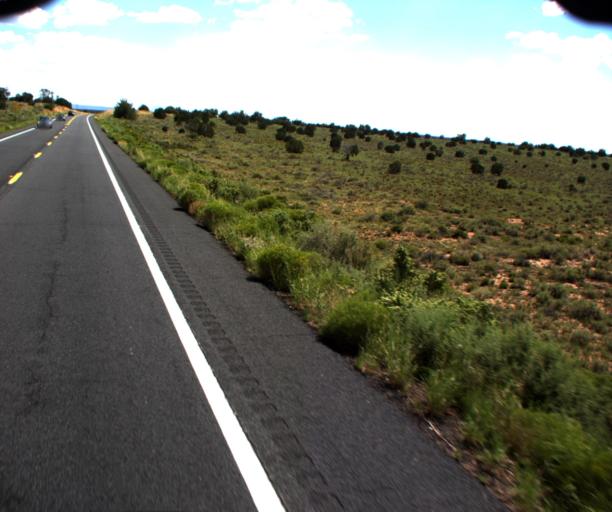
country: US
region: Arizona
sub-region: Coconino County
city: Grand Canyon Village
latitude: 35.7156
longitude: -112.1312
